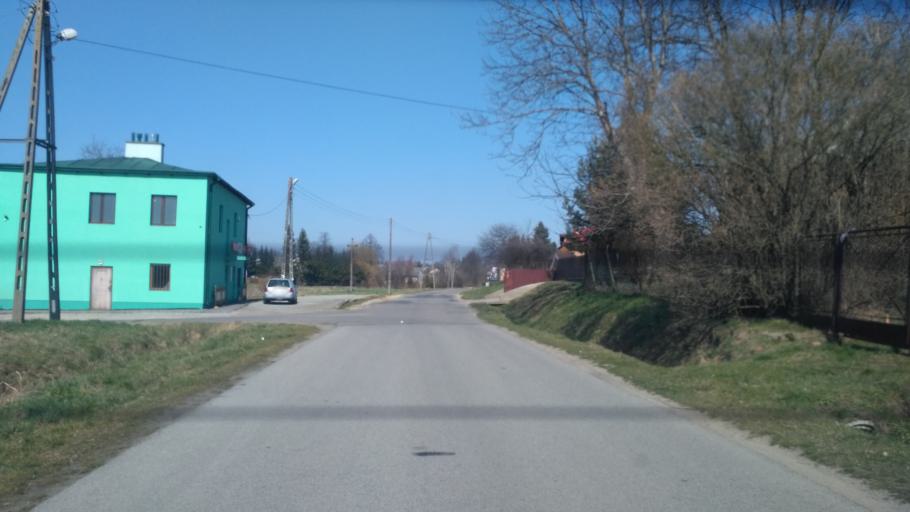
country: PL
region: Subcarpathian Voivodeship
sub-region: Powiat jaroslawski
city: Pawlosiow
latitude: 49.9608
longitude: 22.6504
